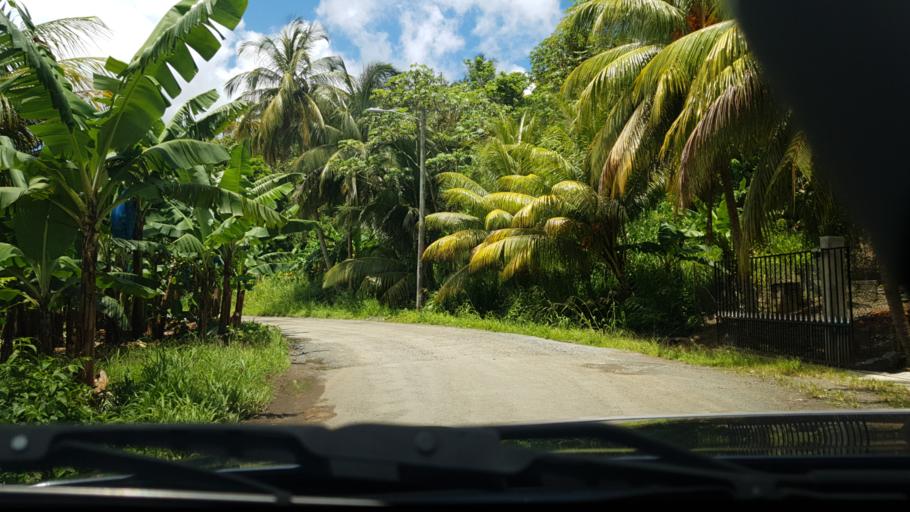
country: LC
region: Anse-la-Raye
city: Anse La Raye
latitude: 13.9530
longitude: -60.9994
